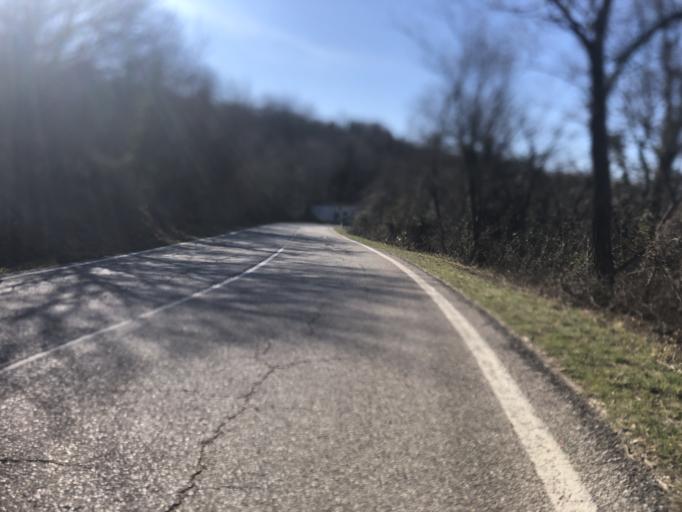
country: IT
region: Veneto
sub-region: Provincia di Verona
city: Volargne
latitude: 45.5440
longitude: 10.8394
